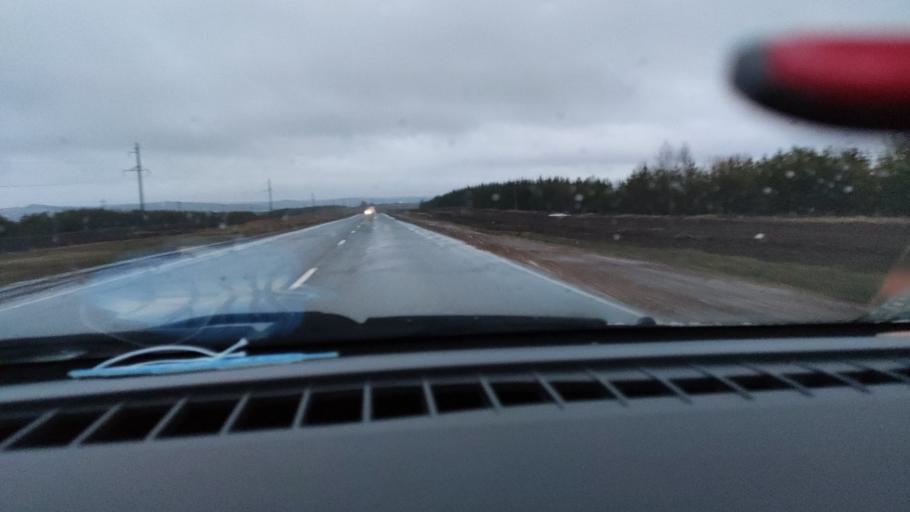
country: RU
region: Udmurtiya
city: Alnashi
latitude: 56.2105
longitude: 52.4373
